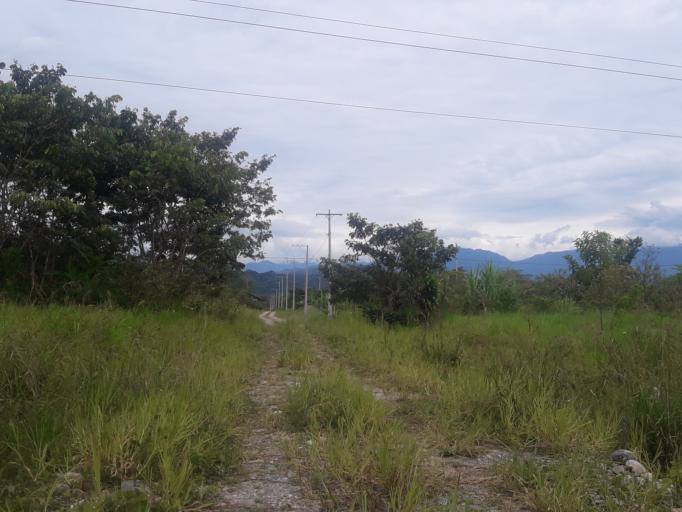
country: EC
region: Napo
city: Tena
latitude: -1.0585
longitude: -77.7938
